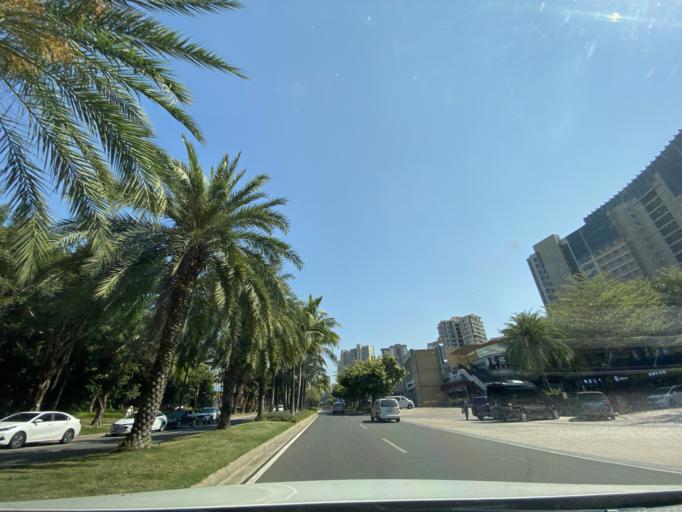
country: CN
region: Hainan
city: Yingzhou
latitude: 18.4025
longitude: 109.8657
